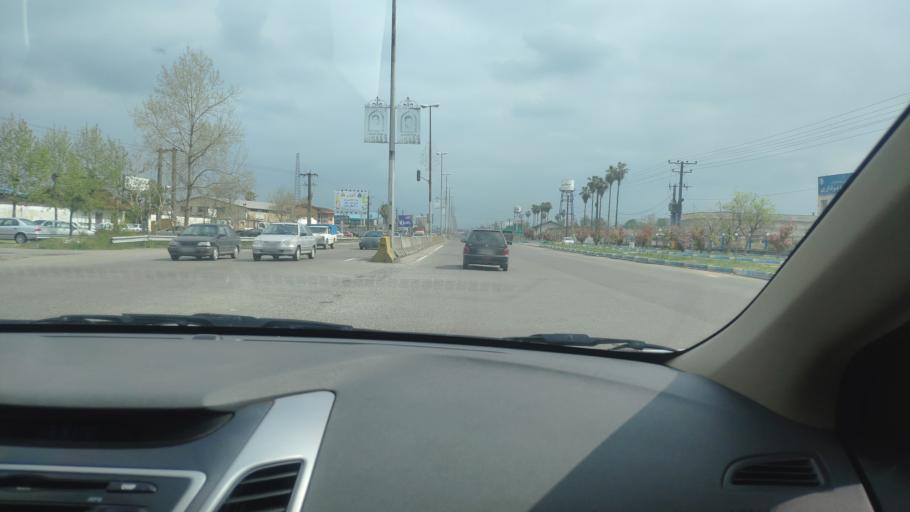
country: IR
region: Gilan
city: Rasht
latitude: 37.2348
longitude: 49.6272
